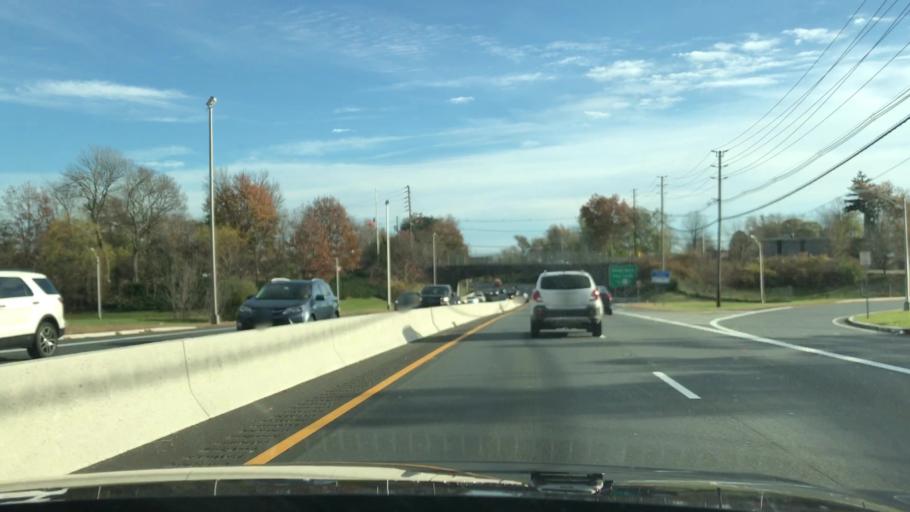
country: US
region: New Jersey
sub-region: Bergen County
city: Fair Lawn
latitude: 40.9391
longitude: -74.1266
